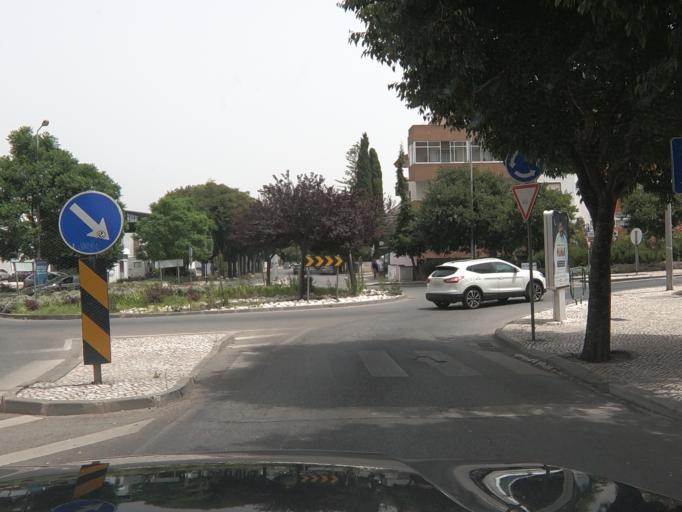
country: PT
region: Faro
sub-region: Portimao
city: Portimao
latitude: 37.1334
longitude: -8.5427
